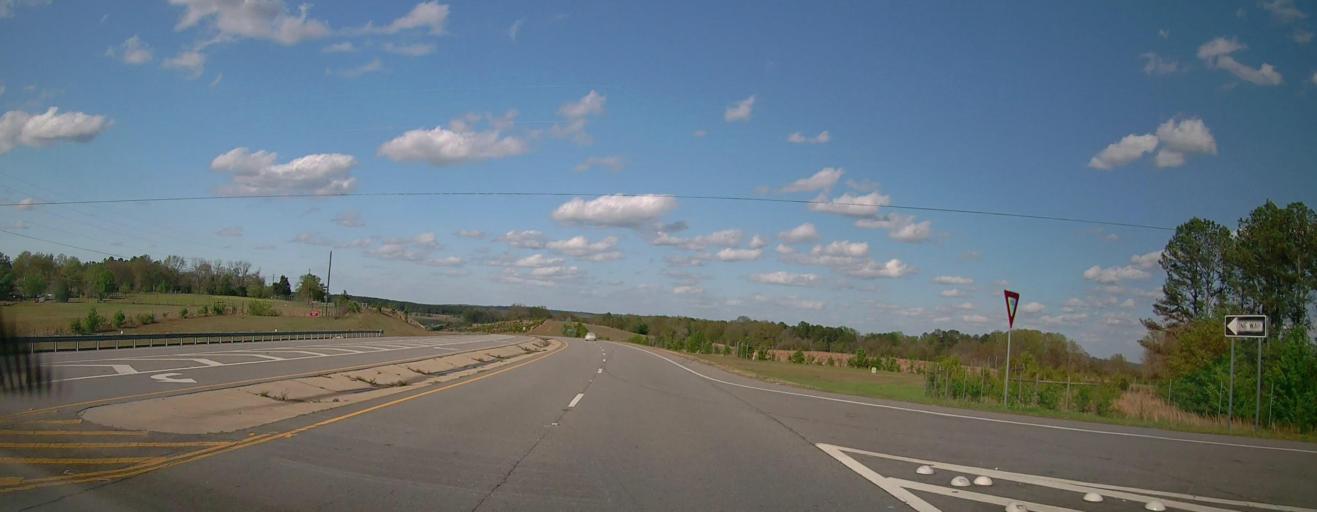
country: US
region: Georgia
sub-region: Baldwin County
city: Hardwick
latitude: 33.0022
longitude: -83.1980
